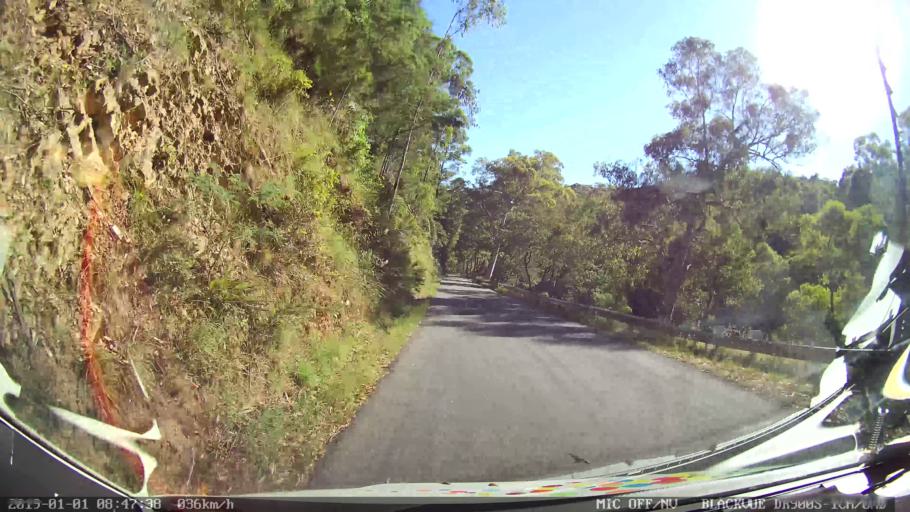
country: AU
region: New South Wales
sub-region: Snowy River
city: Jindabyne
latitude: -36.2933
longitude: 148.1979
